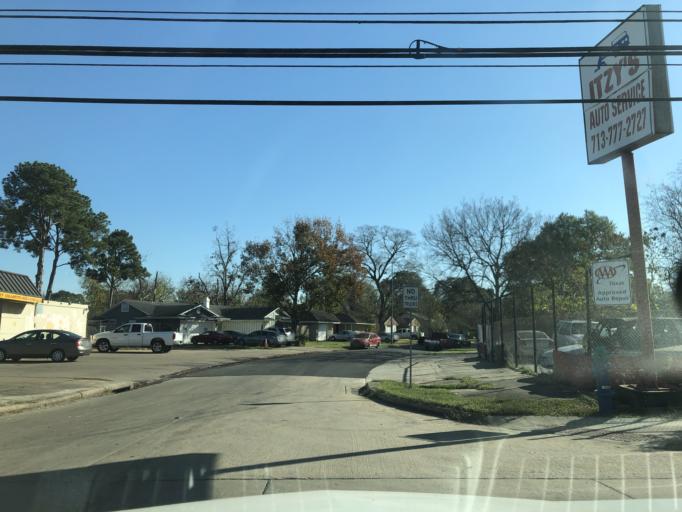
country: US
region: Texas
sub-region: Harris County
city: Bellaire
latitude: 29.6908
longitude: -95.5010
